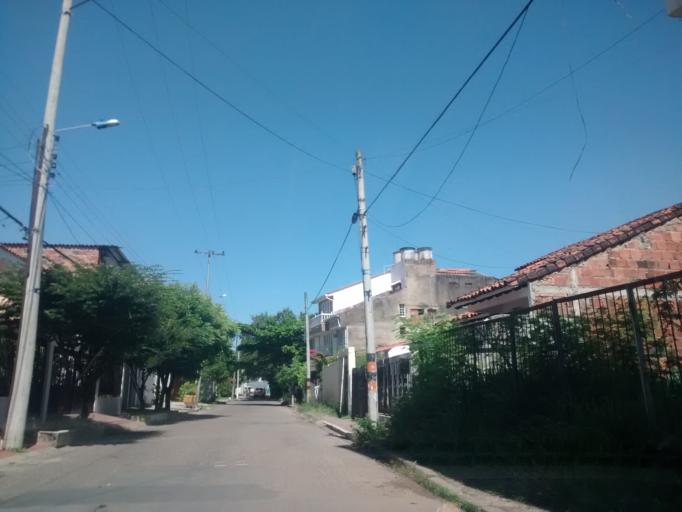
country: CO
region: Cundinamarca
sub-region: Girardot
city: Girardot City
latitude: 4.3065
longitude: -74.8008
